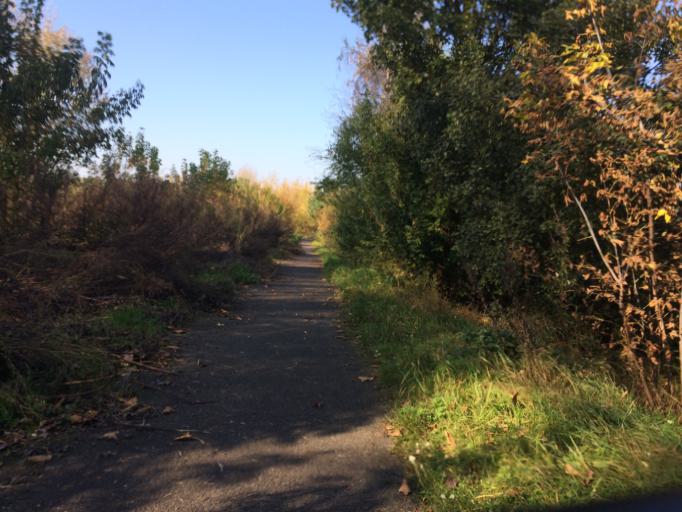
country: DE
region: Berlin
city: Blankenfelde
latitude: 52.6352
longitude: 13.4192
